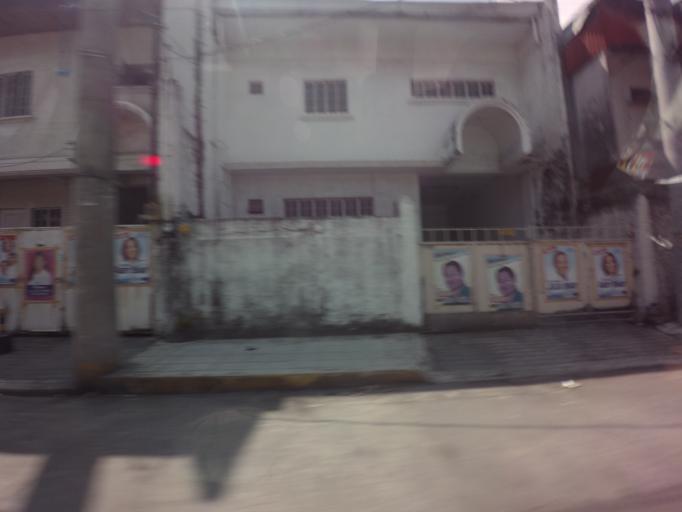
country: PH
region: Metro Manila
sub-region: Makati City
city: Makati City
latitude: 14.5653
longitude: 121.0107
